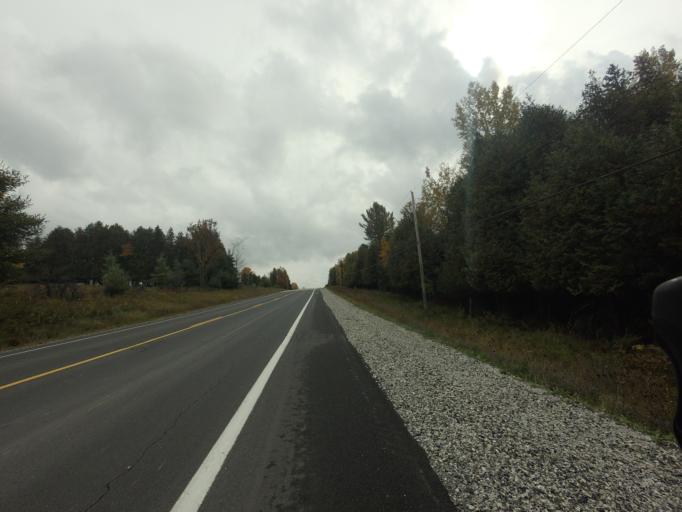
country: CA
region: Ontario
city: Perth
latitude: 45.1018
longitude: -76.4708
